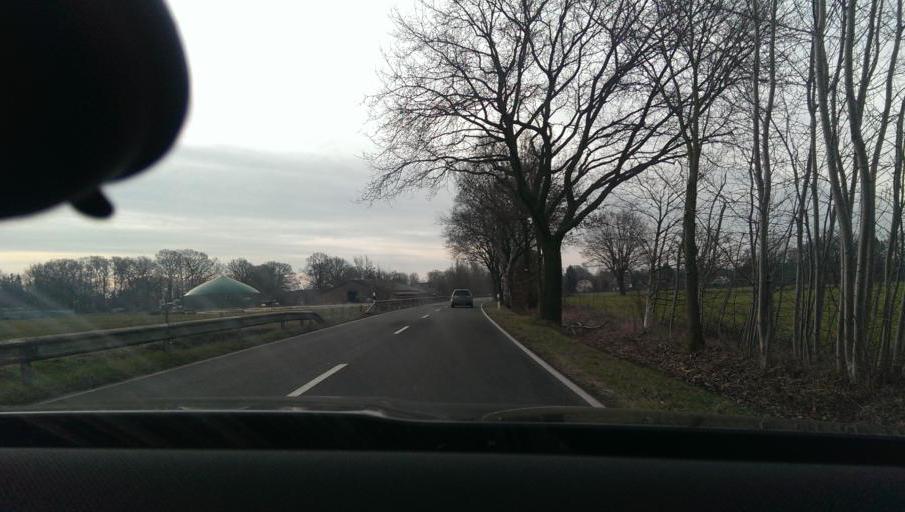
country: DE
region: Lower Saxony
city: Elze
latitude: 52.5563
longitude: 9.7630
